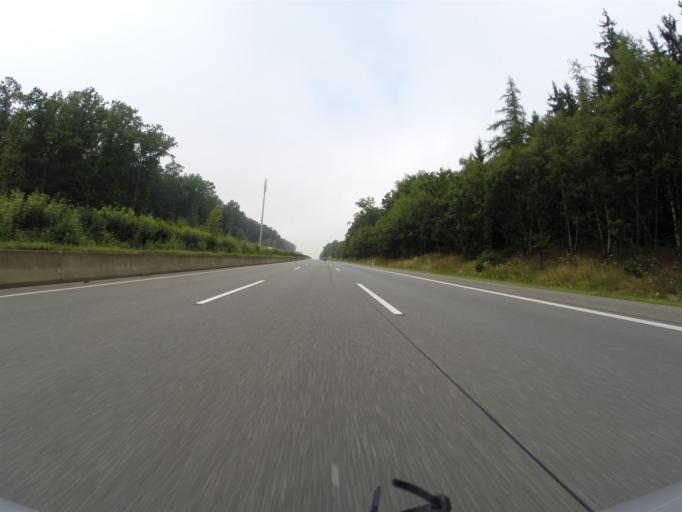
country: DE
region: Thuringia
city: Emleben
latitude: 50.9083
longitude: 10.6529
